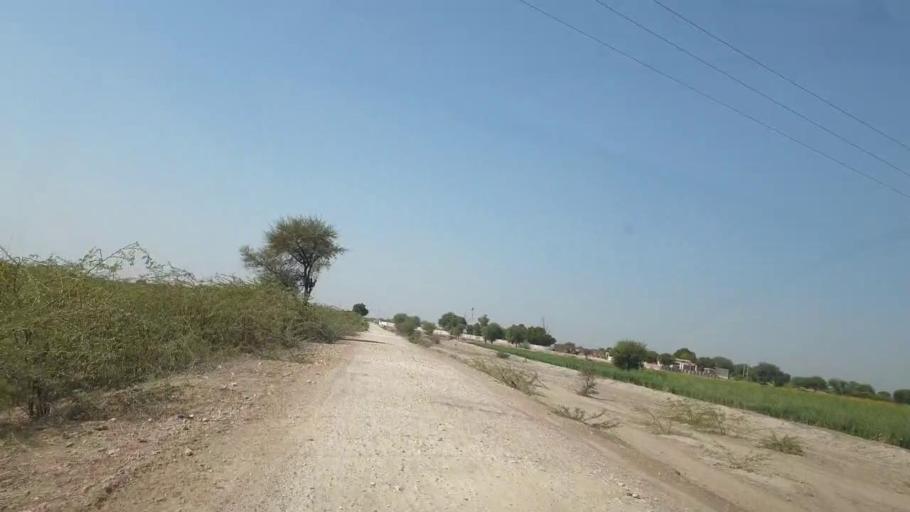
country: PK
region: Sindh
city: Kunri
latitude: 25.1137
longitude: 69.5243
